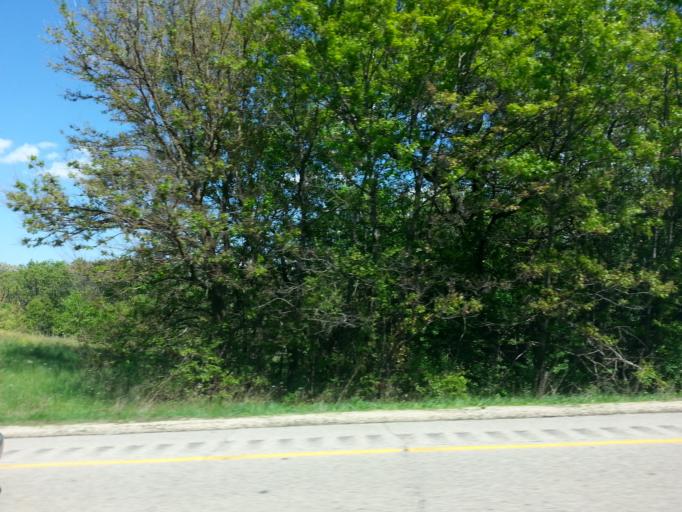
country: US
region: Wisconsin
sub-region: Rock County
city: Milton
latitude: 42.7507
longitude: -89.0054
